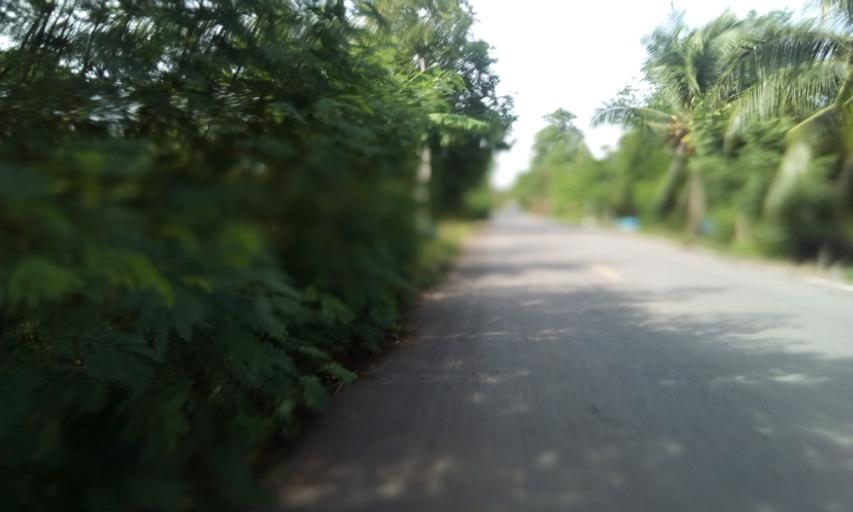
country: TH
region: Pathum Thani
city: Ban Lam Luk Ka
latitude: 14.0184
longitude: 100.8464
